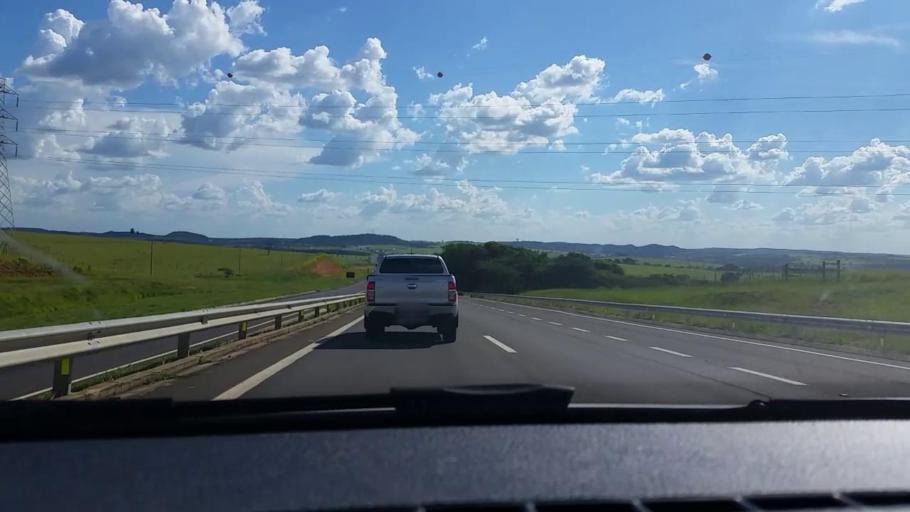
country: BR
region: Sao Paulo
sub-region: Bauru
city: Bauru
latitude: -22.3922
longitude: -49.0800
